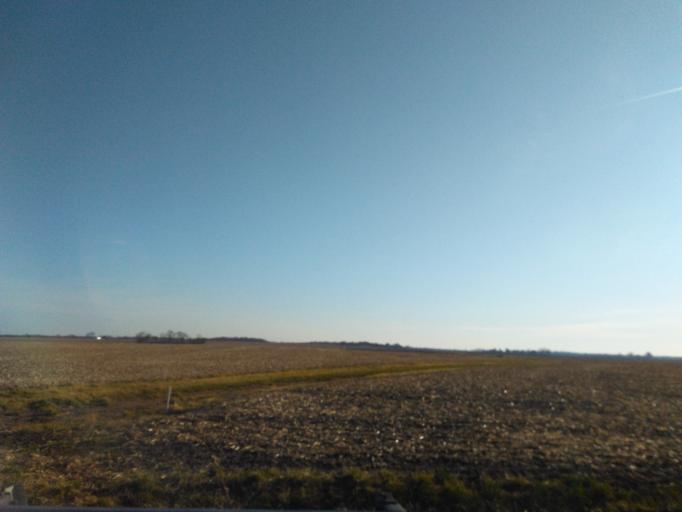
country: US
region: Illinois
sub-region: Madison County
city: Saint Jacob
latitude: 38.7549
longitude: -89.8006
